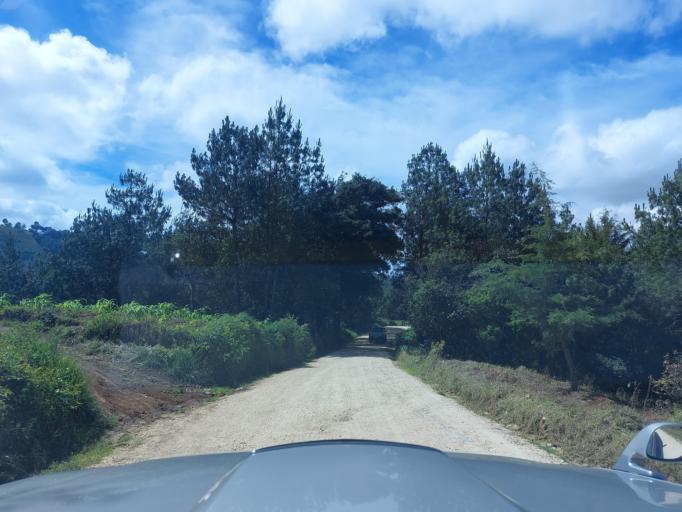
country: GT
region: Chimaltenango
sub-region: Municipio de San Juan Comalapa
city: Comalapa
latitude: 14.7570
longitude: -90.8751
